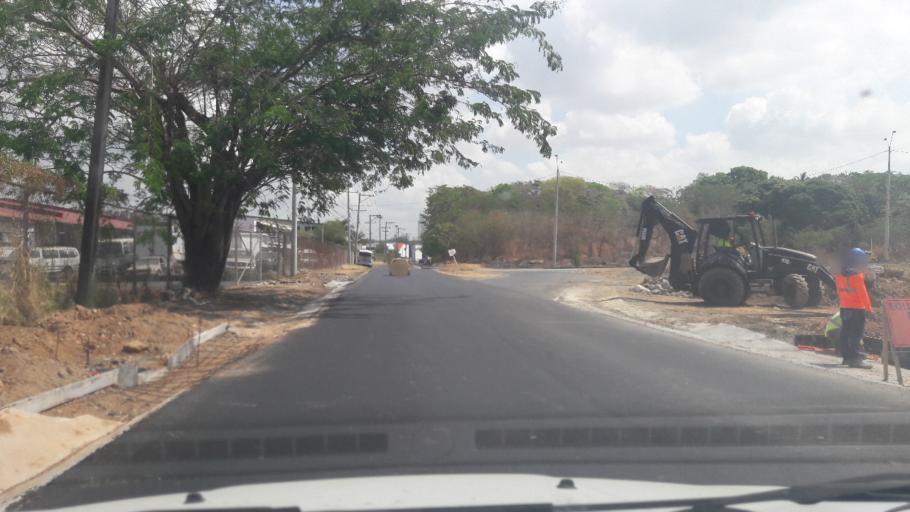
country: PA
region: Panama
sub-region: Distrito de Panama
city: Ancon
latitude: 8.9716
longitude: -79.5468
